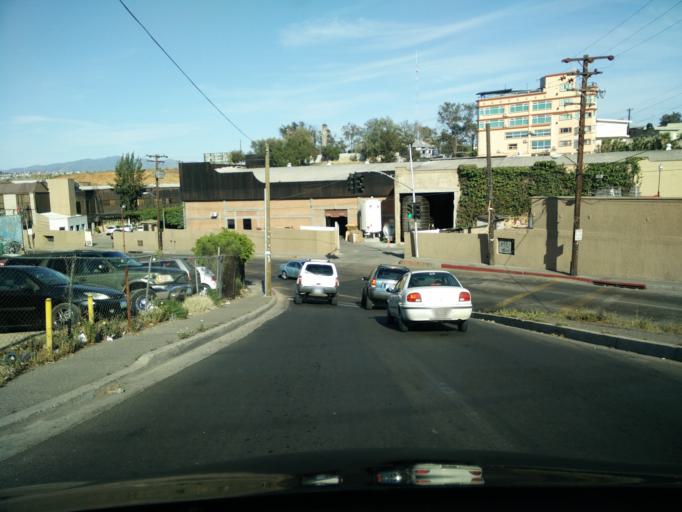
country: MX
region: Baja California
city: Tijuana
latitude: 32.5240
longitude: -117.0387
